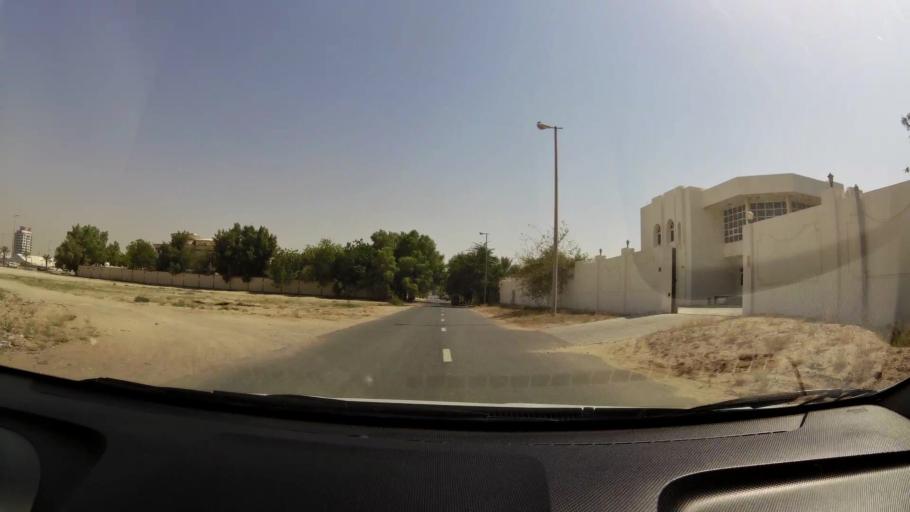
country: AE
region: Ajman
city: Ajman
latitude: 25.4069
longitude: 55.4791
